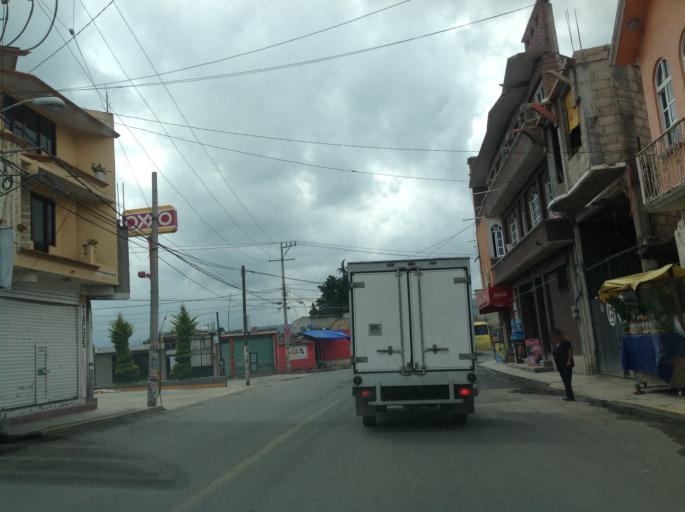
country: MX
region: Mexico
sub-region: Tenango del Valle
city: Santa Maria Jajalpa
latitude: 19.1150
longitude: -99.5382
